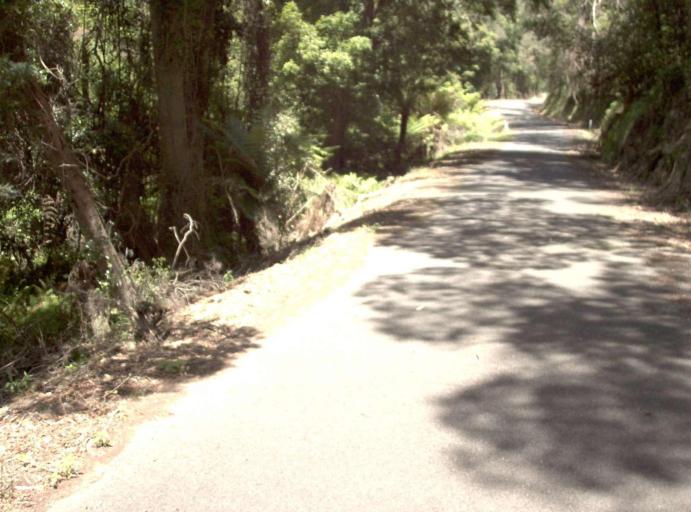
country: AU
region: New South Wales
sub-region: Bombala
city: Bombala
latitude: -37.4576
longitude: 148.9365
